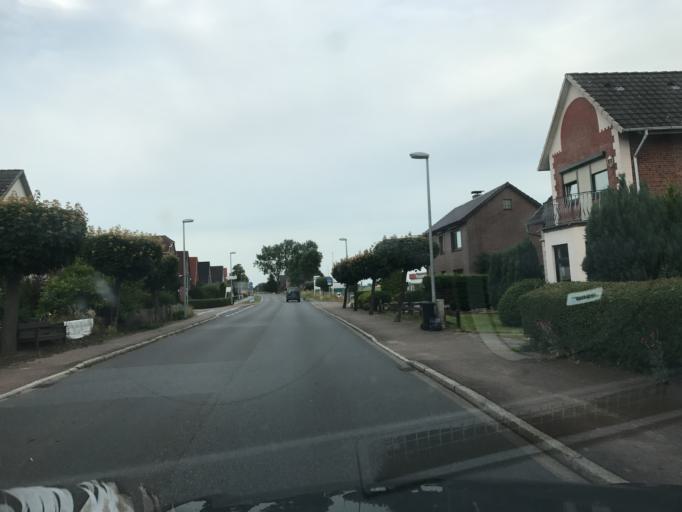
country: DE
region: Schleswig-Holstein
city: Wilster
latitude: 53.9240
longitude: 9.3836
